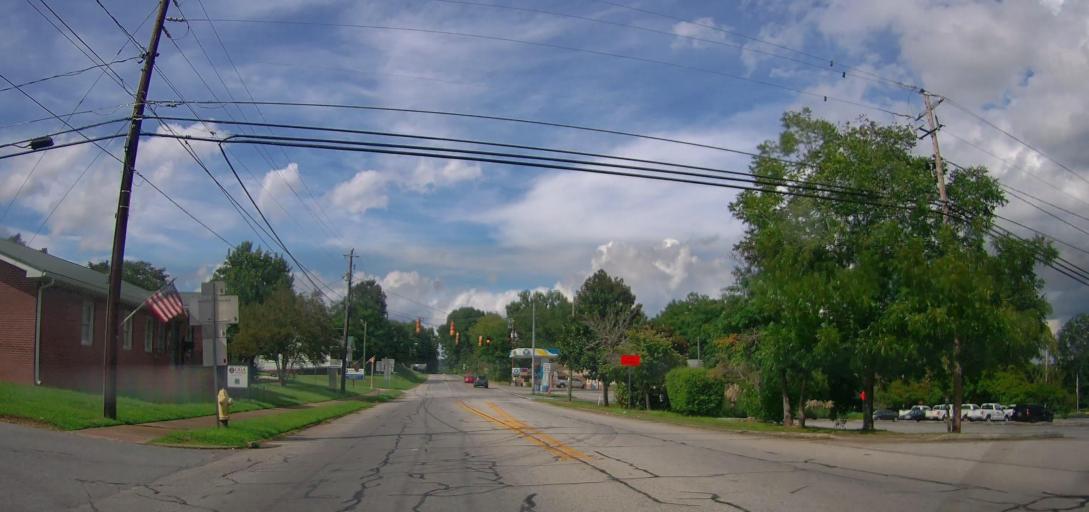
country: US
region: Georgia
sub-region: Harris County
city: Hamilton
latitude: 32.7591
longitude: -84.8751
